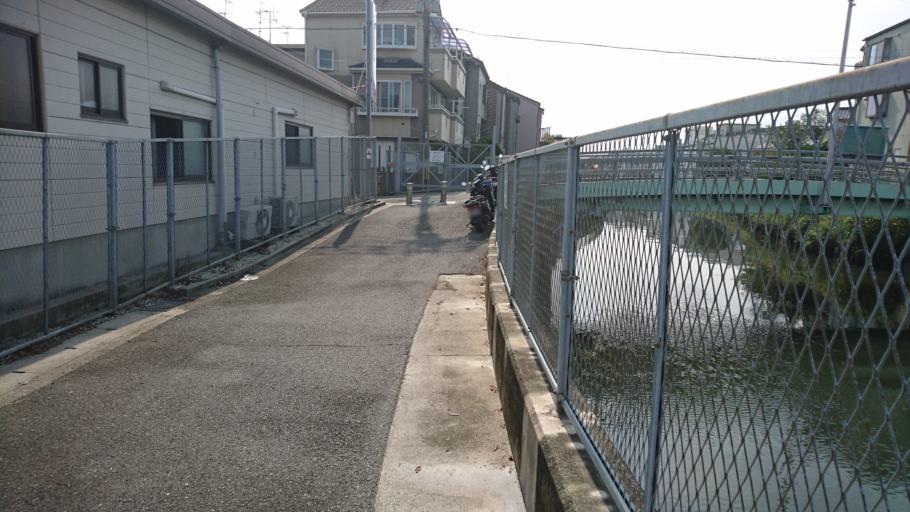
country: JP
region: Osaka
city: Kadoma
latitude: 34.7100
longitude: 135.5869
